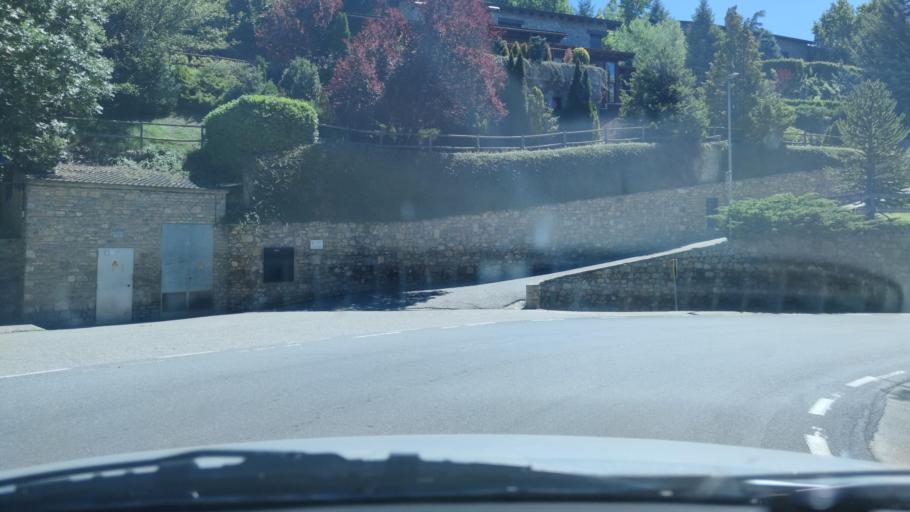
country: ES
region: Catalonia
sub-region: Provincia de Lleida
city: Bellver de Cerdanya
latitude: 42.3770
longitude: 1.7413
